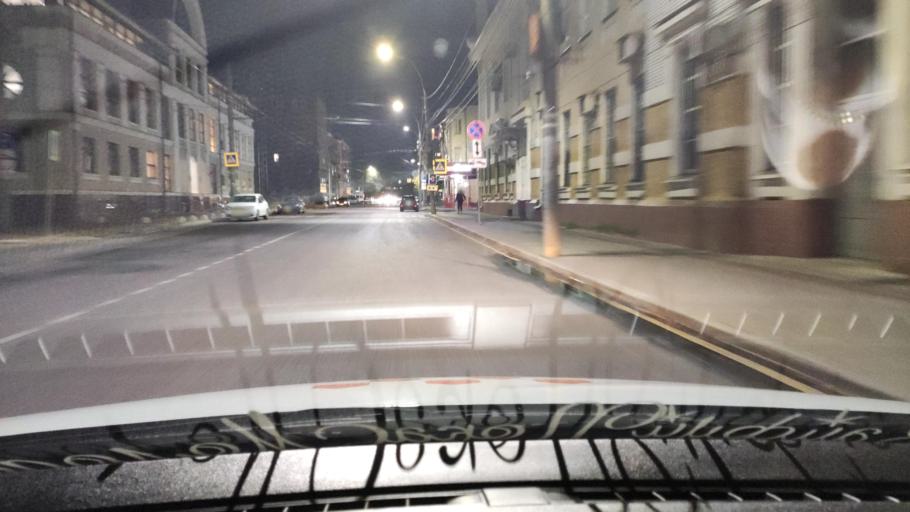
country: RU
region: Voronezj
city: Voronezh
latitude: 51.6582
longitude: 39.2014
